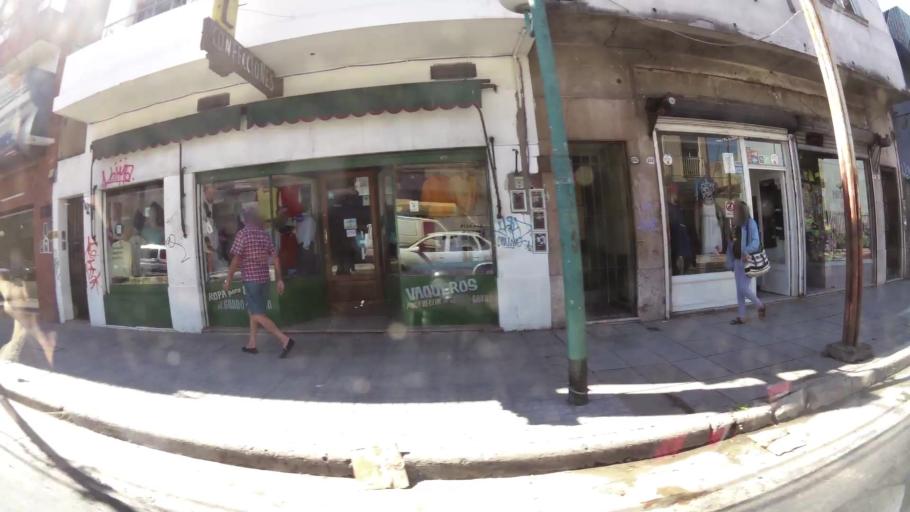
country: AR
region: Buenos Aires
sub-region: Partido de General San Martin
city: General San Martin
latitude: -34.5318
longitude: -58.5270
